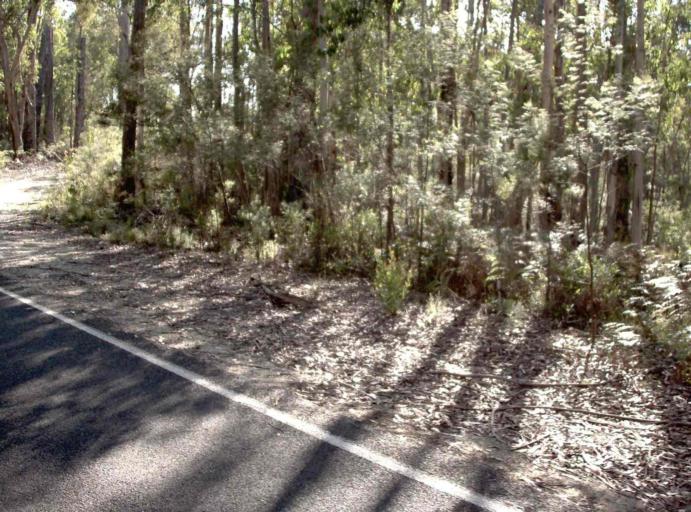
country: AU
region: Victoria
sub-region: East Gippsland
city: Lakes Entrance
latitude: -37.5706
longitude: 148.5493
